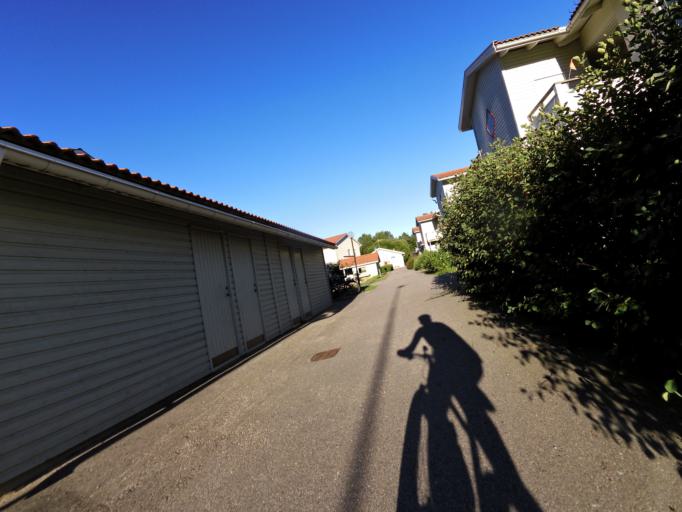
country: SE
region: Gaevleborg
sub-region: Gavle Kommun
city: Gavle
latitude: 60.6603
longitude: 17.1491
